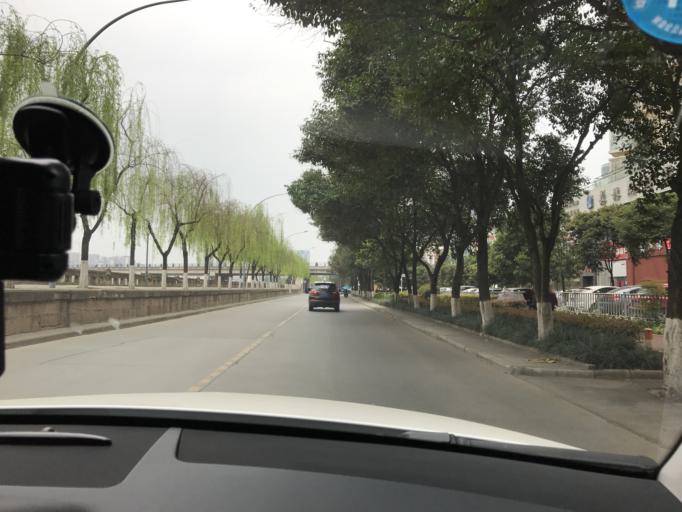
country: CN
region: Sichuan
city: Mianyang
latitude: 31.4543
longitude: 104.7088
